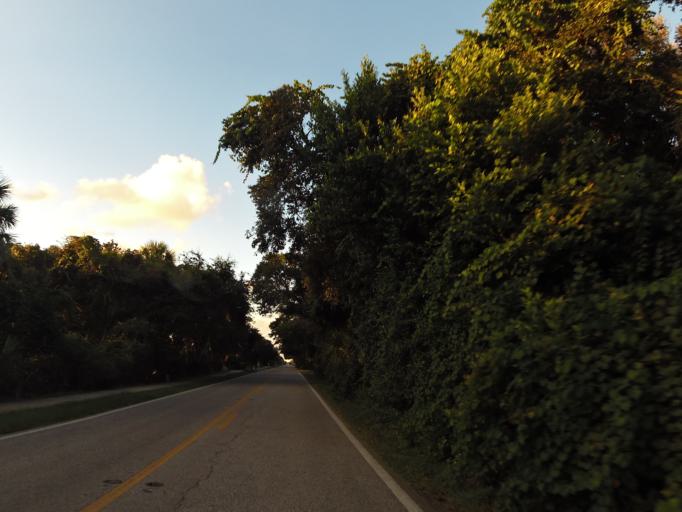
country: US
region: Florida
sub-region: Saint Johns County
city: Sawgrass
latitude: 30.1653
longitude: -81.3580
